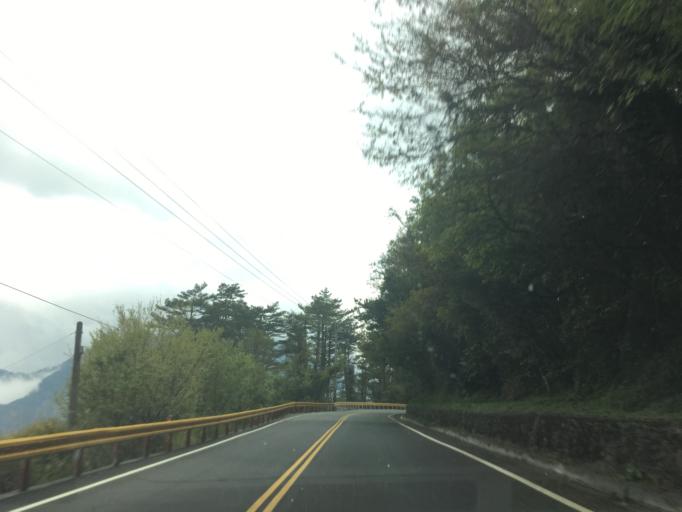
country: TW
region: Taiwan
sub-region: Hualien
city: Hualian
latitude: 24.1842
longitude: 121.3267
